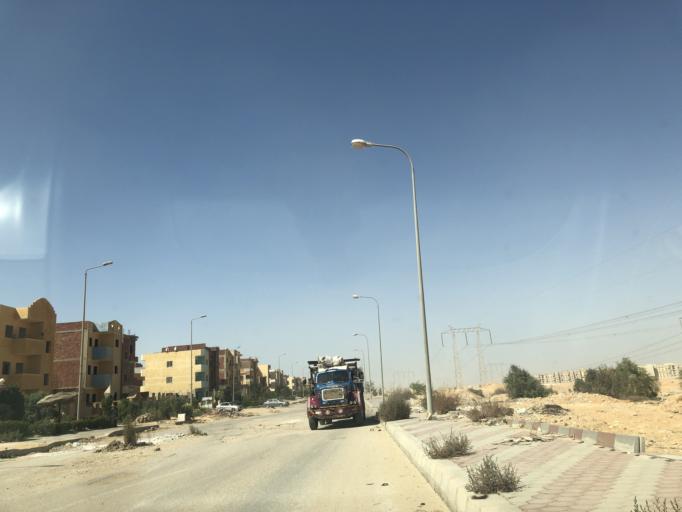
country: EG
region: Al Jizah
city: Madinat Sittah Uktubar
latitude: 29.9128
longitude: 31.0500
